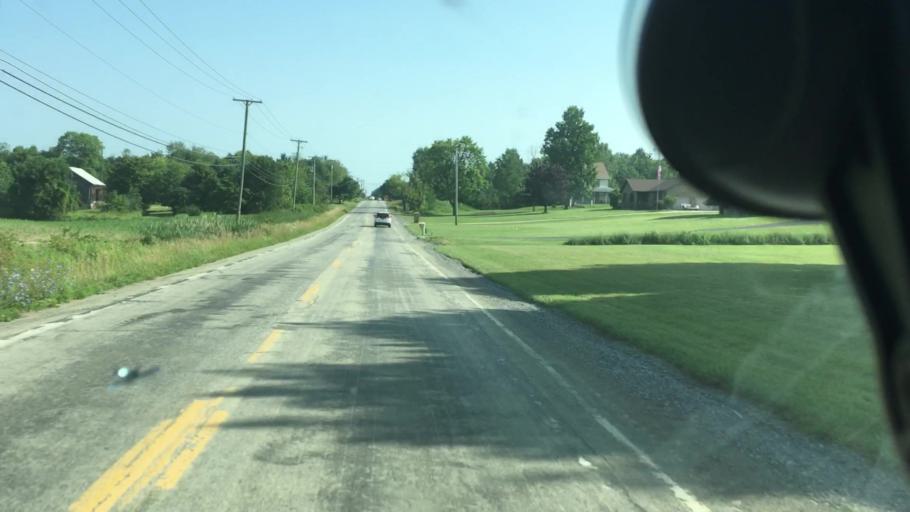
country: US
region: Pennsylvania
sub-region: Lawrence County
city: New Castle
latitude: 41.0072
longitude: -80.2700
